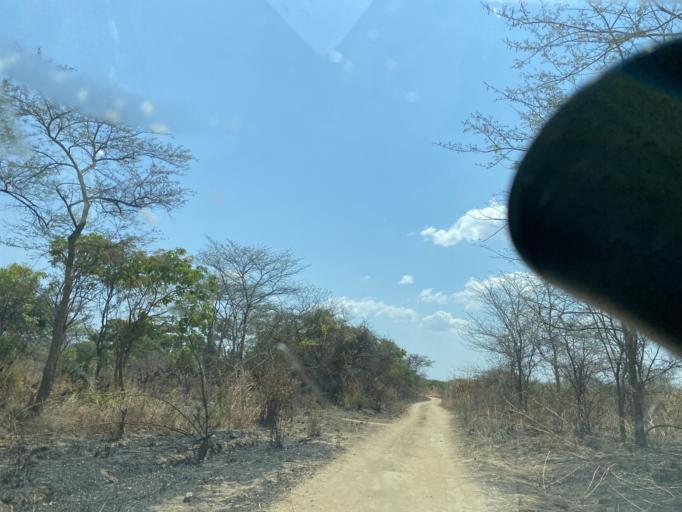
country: ZM
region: Lusaka
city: Chongwe
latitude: -15.0810
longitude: 29.5107
